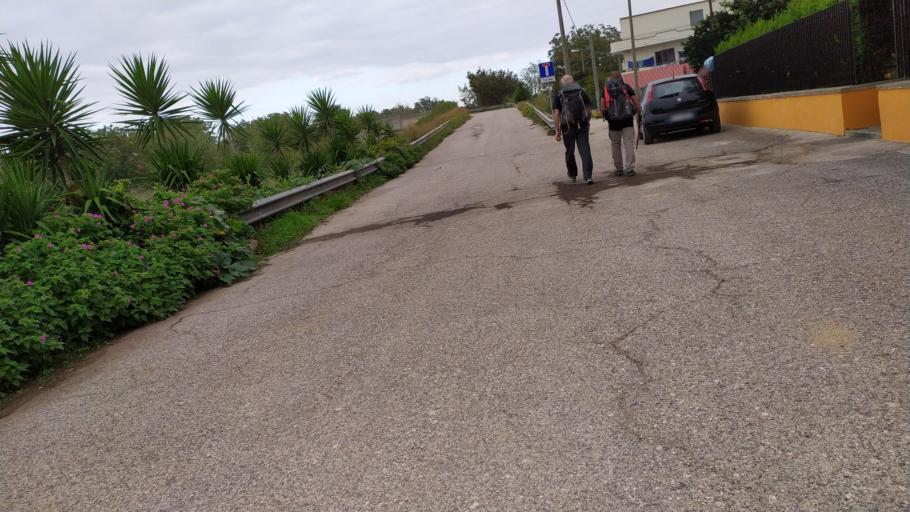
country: IT
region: Campania
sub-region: Provincia di Caserta
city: Montedecoro
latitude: 41.0095
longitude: 14.4110
